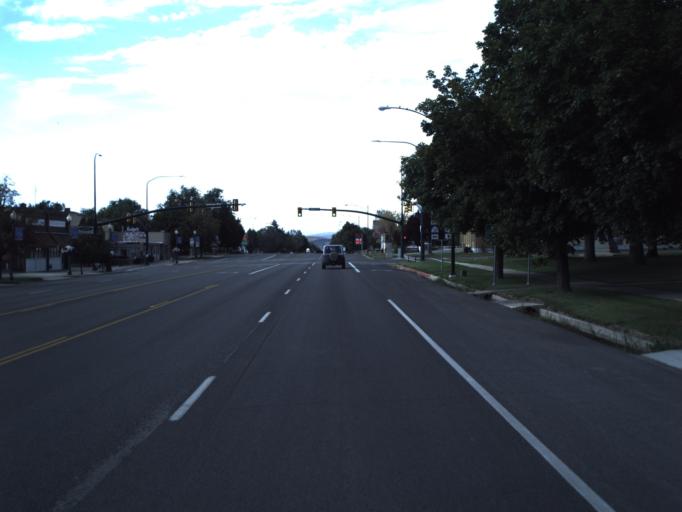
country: US
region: Utah
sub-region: Sanpete County
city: Mount Pleasant
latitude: 39.5458
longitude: -111.4553
